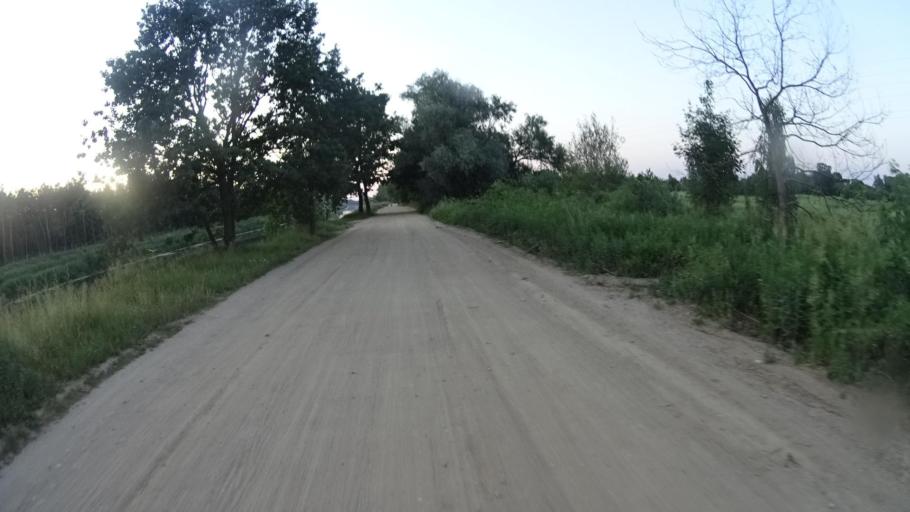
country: PL
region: Masovian Voivodeship
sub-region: Powiat legionowski
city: Stanislawow Pierwszy
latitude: 52.3484
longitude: 21.0343
